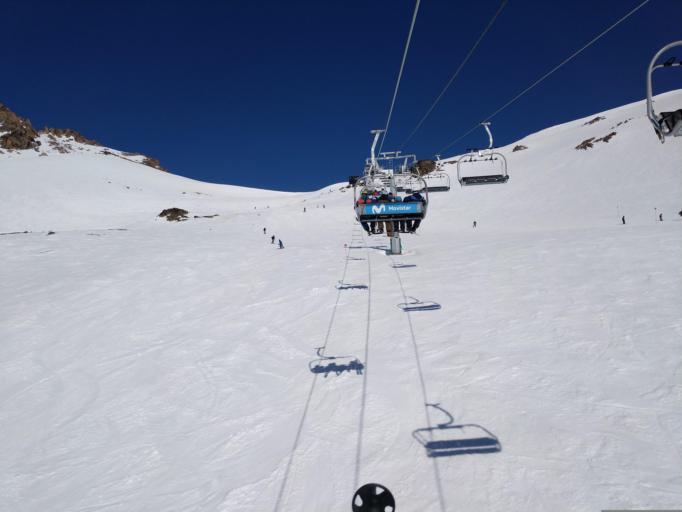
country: AR
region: Rio Negro
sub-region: Departamento de Bariloche
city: San Carlos de Bariloche
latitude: -41.1718
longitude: -71.4812
